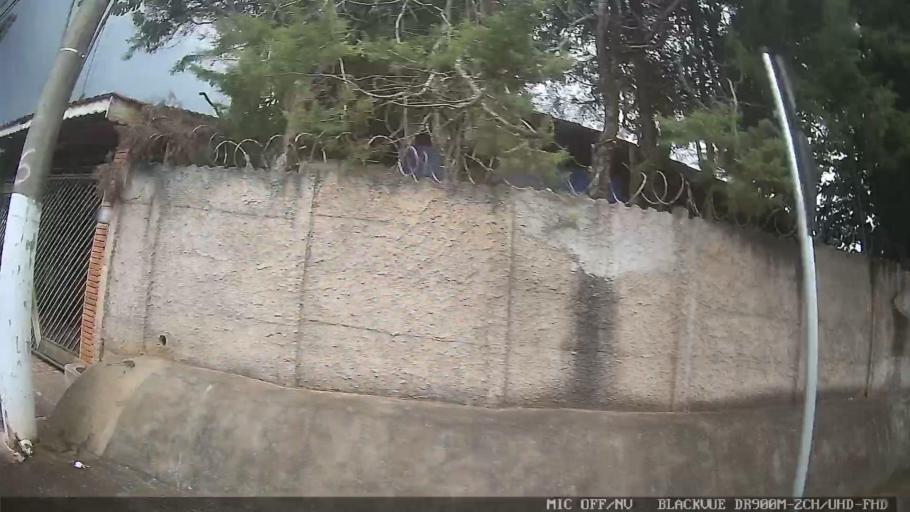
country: BR
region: Sao Paulo
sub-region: Atibaia
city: Atibaia
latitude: -23.1517
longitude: -46.5837
